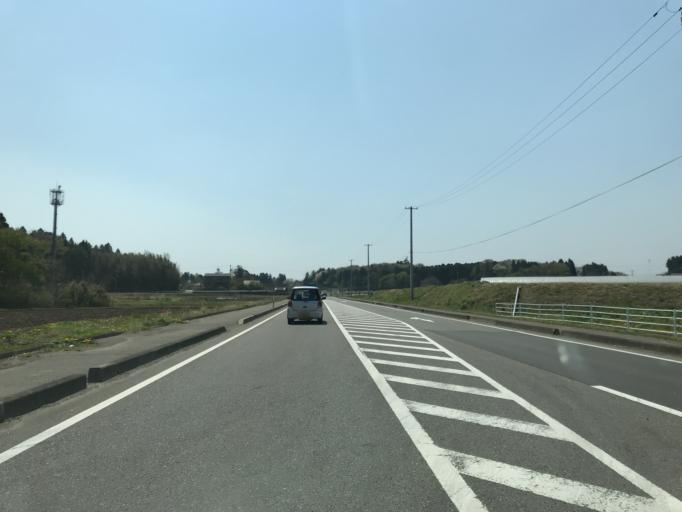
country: JP
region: Fukushima
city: Ishikawa
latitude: 37.1747
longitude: 140.3492
